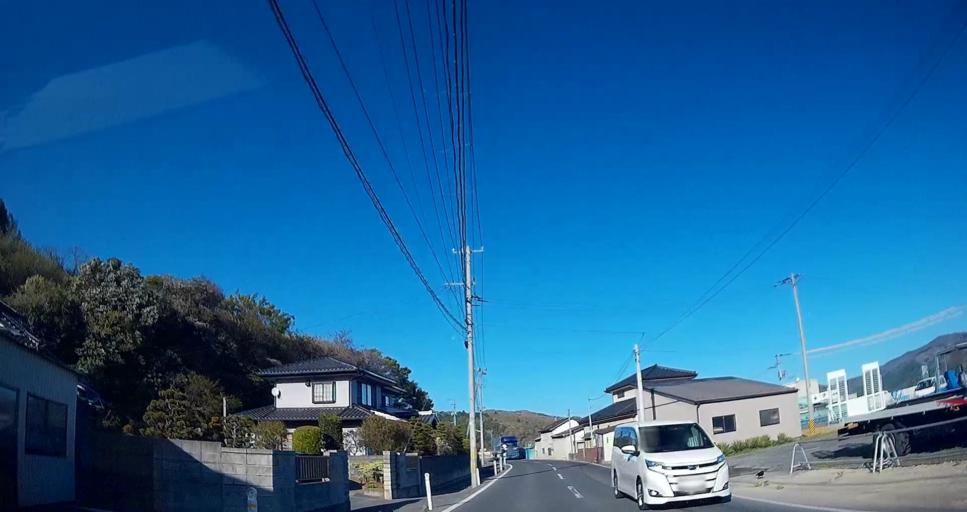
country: JP
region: Miyagi
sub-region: Oshika Gun
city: Onagawa Cho
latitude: 38.4335
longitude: 141.3830
